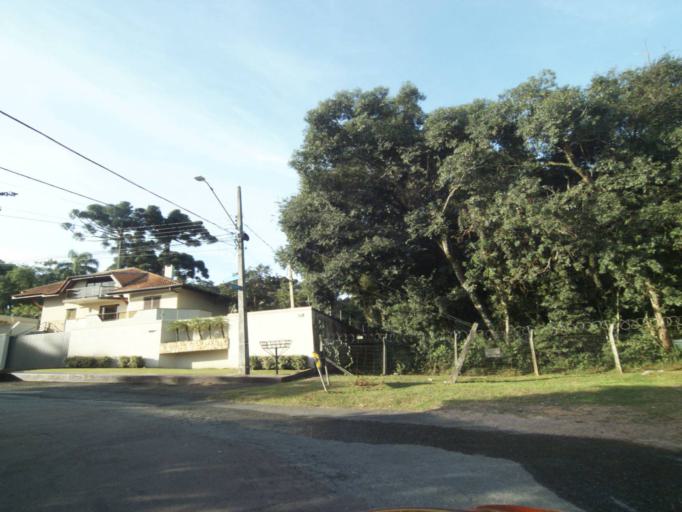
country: BR
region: Parana
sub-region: Curitiba
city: Curitiba
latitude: -25.4325
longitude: -49.3063
